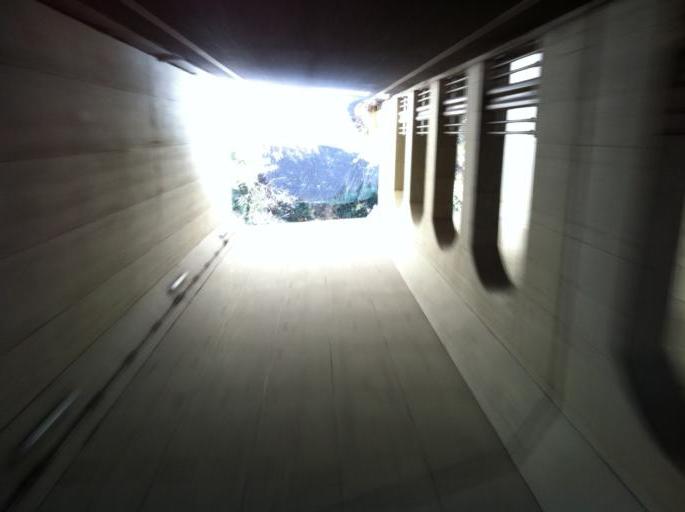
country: JP
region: Shizuoka
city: Yaizu
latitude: 34.9280
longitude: 138.3023
